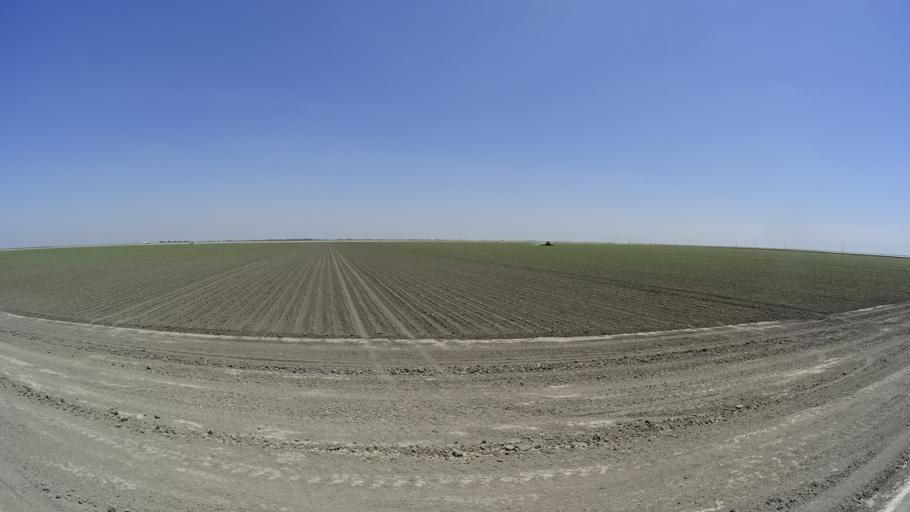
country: US
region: California
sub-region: Kings County
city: Corcoran
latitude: 36.0833
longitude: -119.6440
